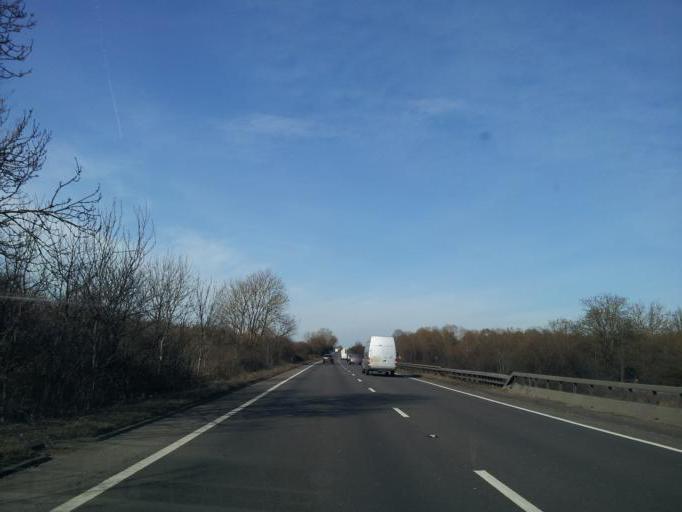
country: GB
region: England
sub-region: District of Rutland
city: Clipsham
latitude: 52.7140
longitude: -0.5932
